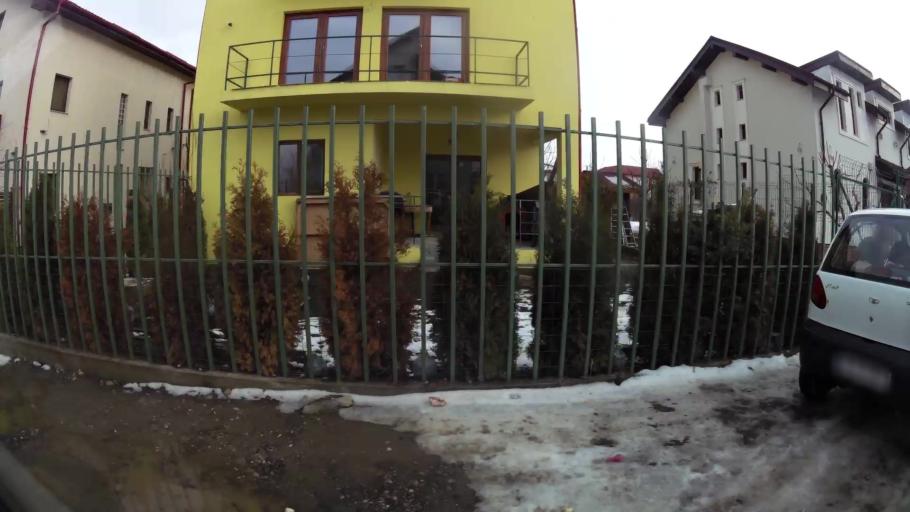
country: RO
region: Ilfov
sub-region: Comuna Popesti-Leordeni
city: Popesti-Leordeni
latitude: 44.4033
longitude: 26.1828
